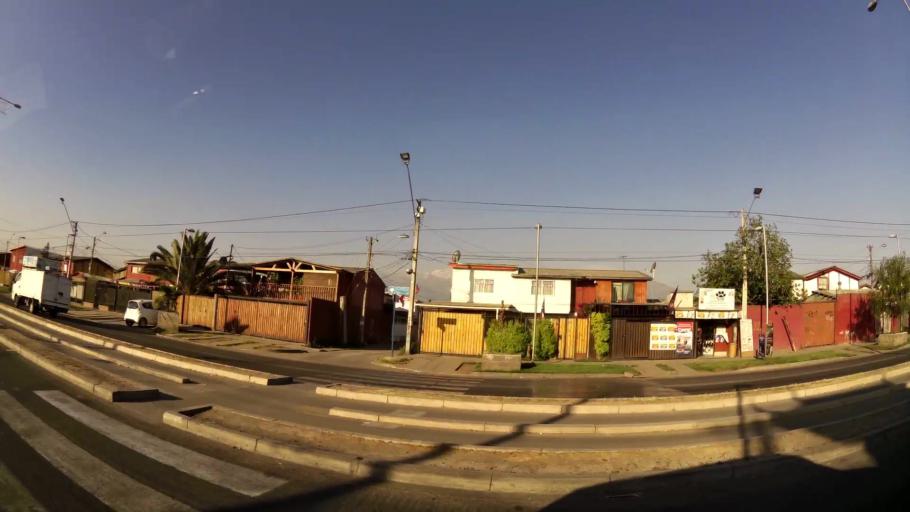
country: CL
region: Santiago Metropolitan
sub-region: Provincia de Santiago
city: La Pintana
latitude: -33.5512
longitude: -70.6178
